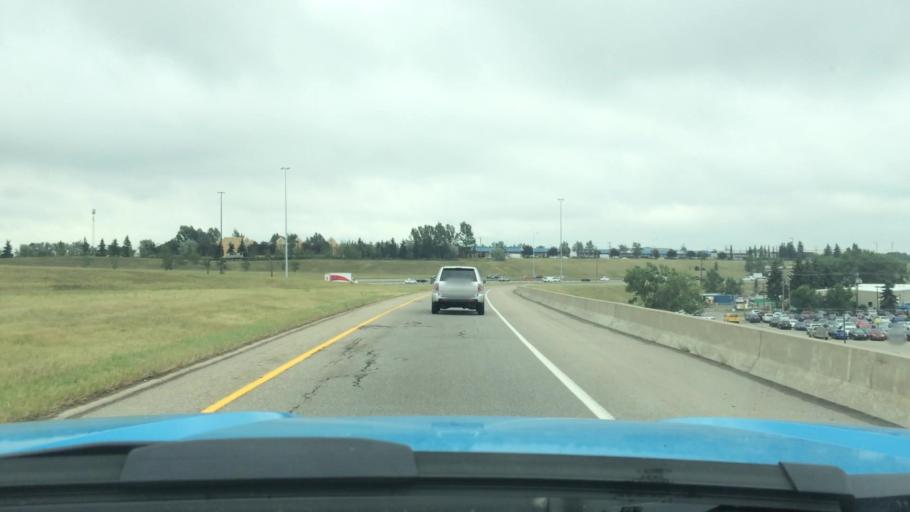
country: CA
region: Alberta
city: Calgary
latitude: 51.0955
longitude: -114.0436
